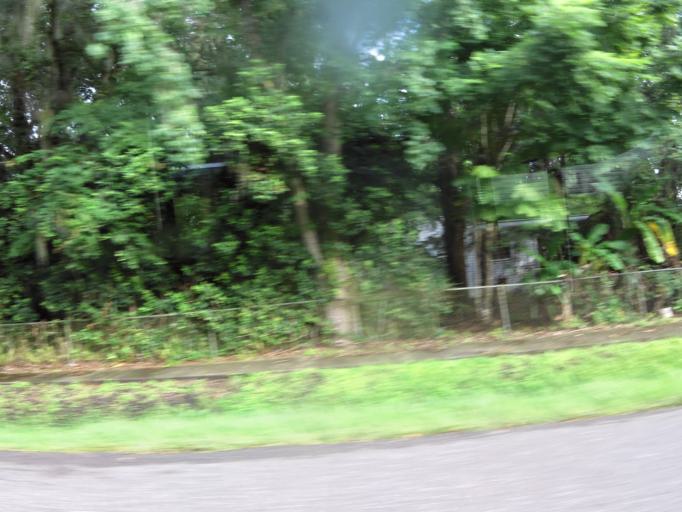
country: US
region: Florida
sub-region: Nassau County
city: Nassau Village-Ratliff
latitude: 30.4268
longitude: -81.7655
